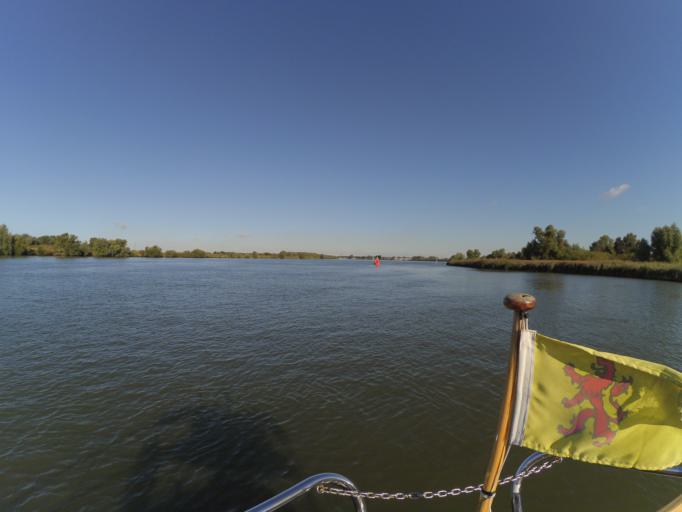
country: NL
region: South Holland
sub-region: Gemeente Zwijndrecht
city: Heerjansdam
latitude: 51.8180
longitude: 4.5622
